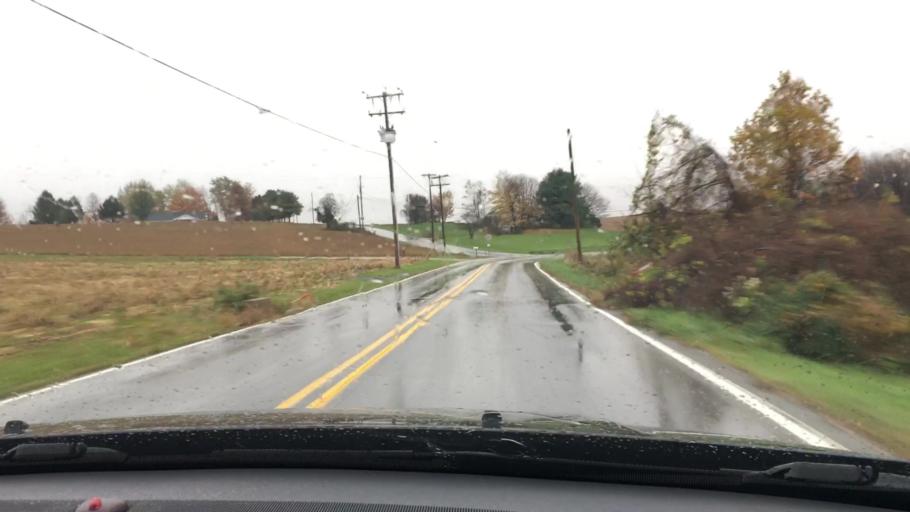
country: US
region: Pennsylvania
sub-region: York County
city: Susquehanna Trails
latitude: 39.7607
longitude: -76.4696
